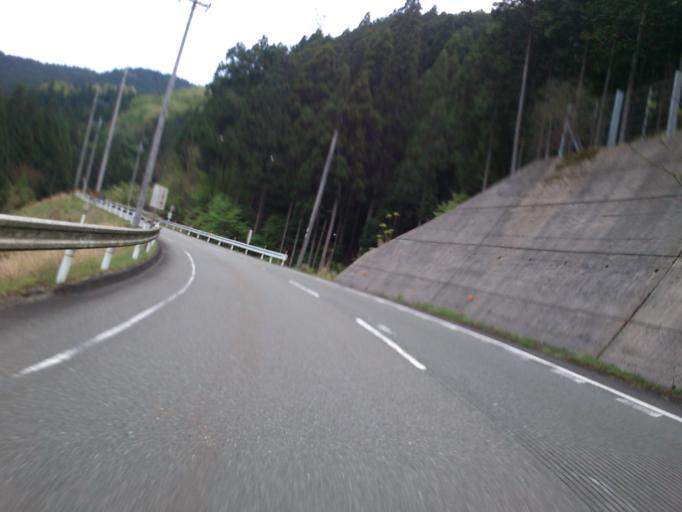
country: JP
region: Kyoto
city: Fukuchiyama
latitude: 35.3055
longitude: 135.0098
